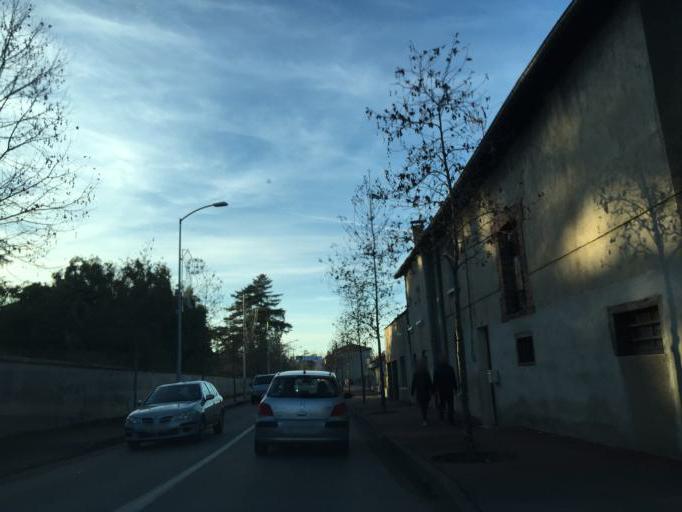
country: FR
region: Rhone-Alpes
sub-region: Departement de la Loire
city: Andrezieux-Boutheon
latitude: 45.5296
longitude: 4.2552
